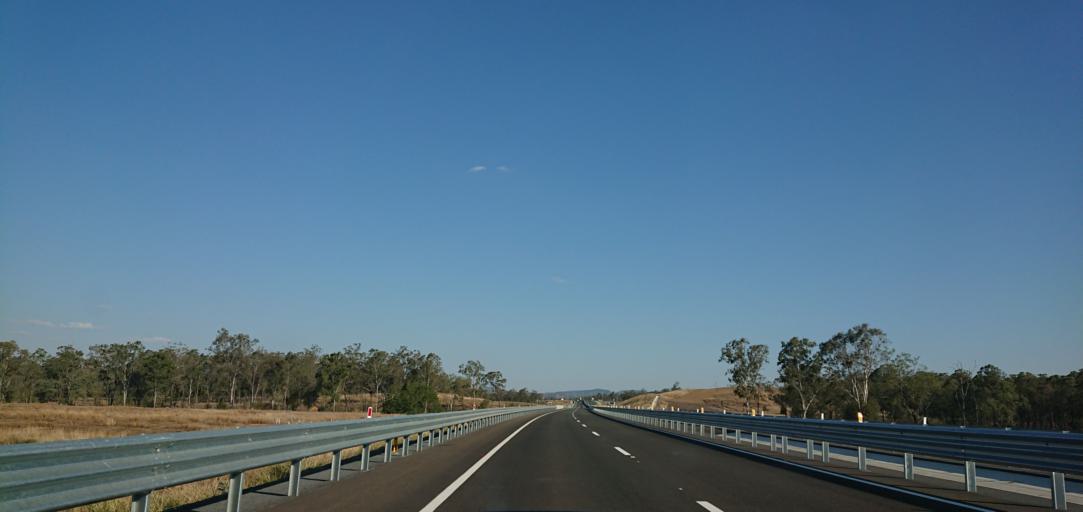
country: AU
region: Queensland
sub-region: Toowoomba
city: Rangeville
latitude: -27.5342
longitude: 152.0755
